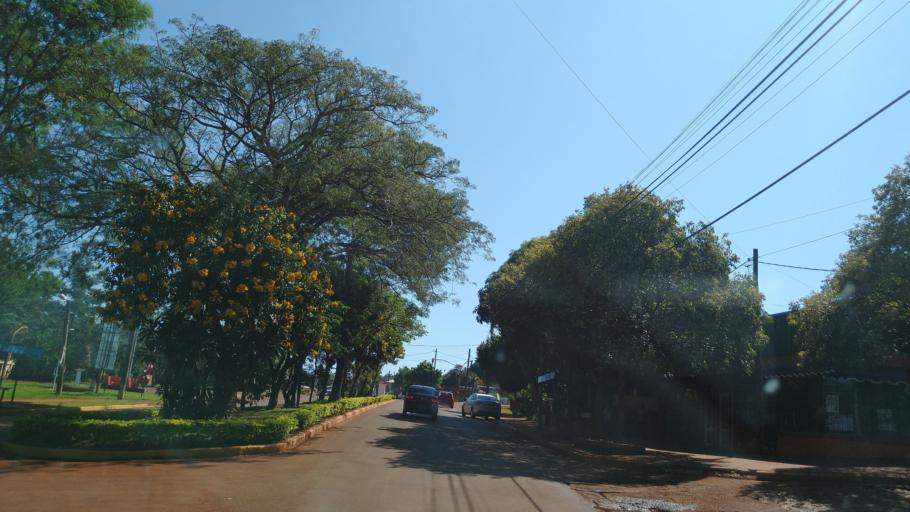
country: AR
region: Misiones
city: Puerto Libertad
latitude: -25.9705
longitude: -54.5609
